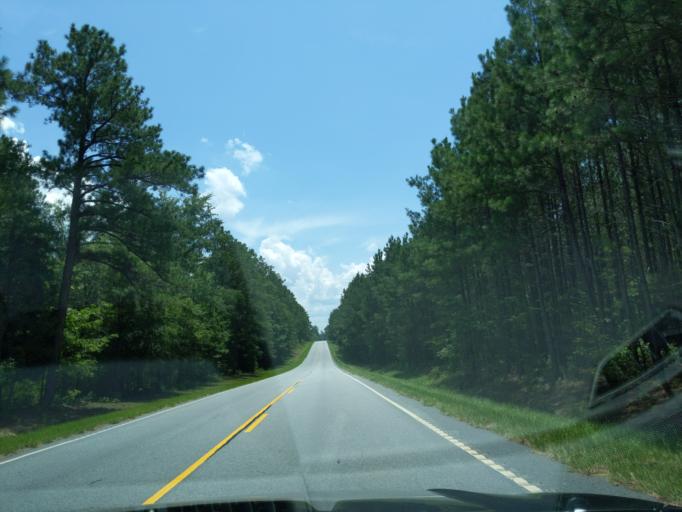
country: US
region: South Carolina
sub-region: Greenwood County
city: Ninety Six
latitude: 33.9685
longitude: -82.0461
